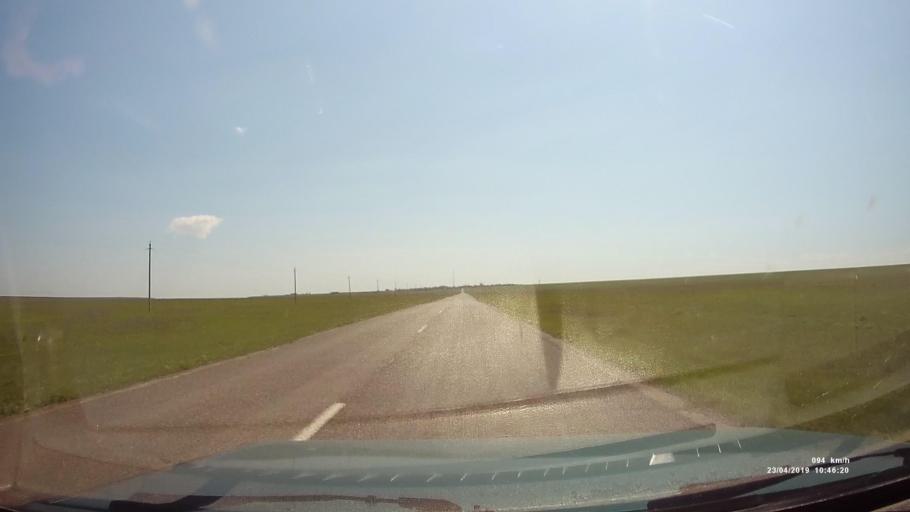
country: RU
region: Kalmykiya
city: Yashalta
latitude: 46.4438
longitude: 42.6895
